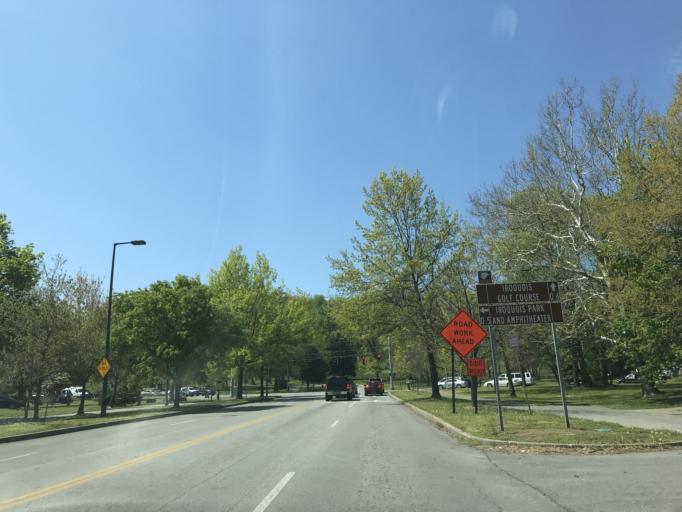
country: US
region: Kentucky
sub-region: Jefferson County
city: Shively
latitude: 38.1705
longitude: -85.7804
